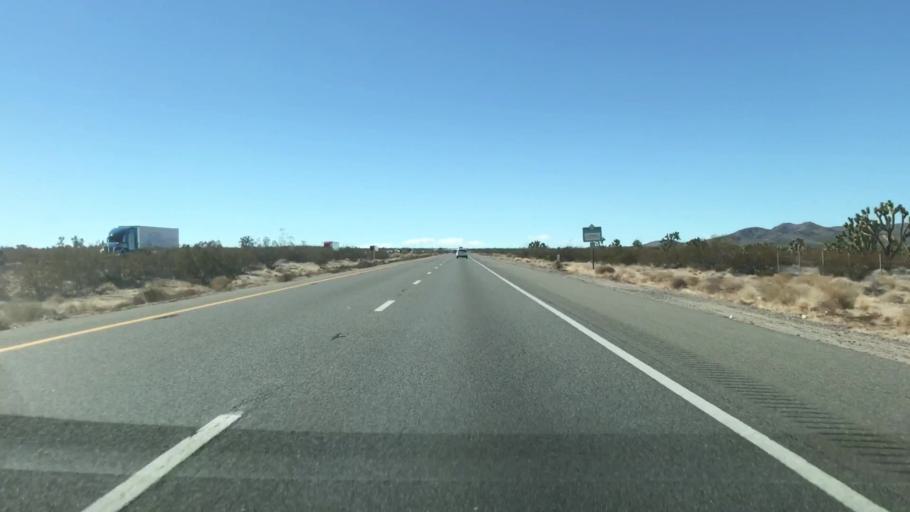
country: US
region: Nevada
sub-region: Clark County
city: Sandy Valley
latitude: 35.4170
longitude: -115.7516
